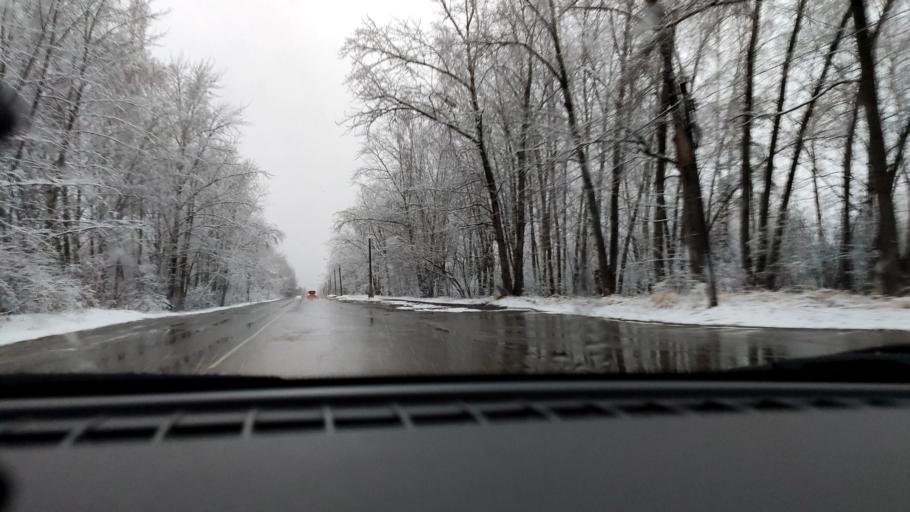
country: RU
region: Perm
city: Overyata
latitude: 58.0147
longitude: 55.9052
